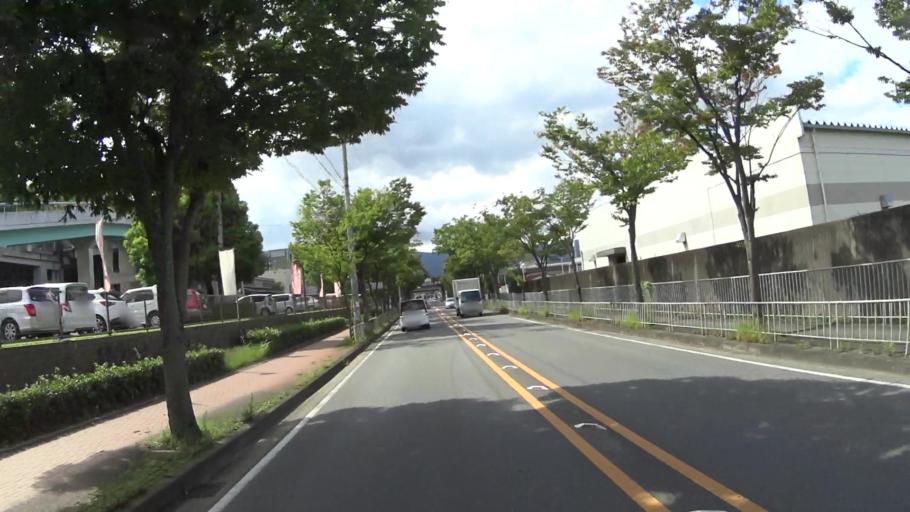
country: JP
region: Kyoto
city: Yawata
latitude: 34.9098
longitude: 135.7076
